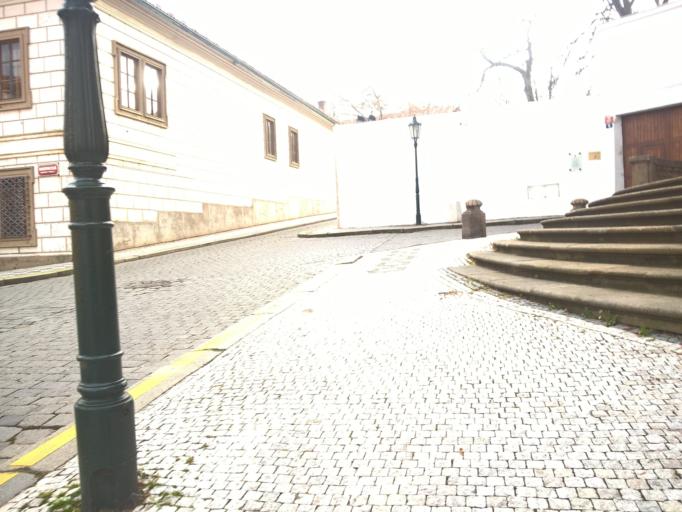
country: CZ
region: Praha
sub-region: Praha 1
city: Mala Strana
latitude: 50.0904
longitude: 14.3935
